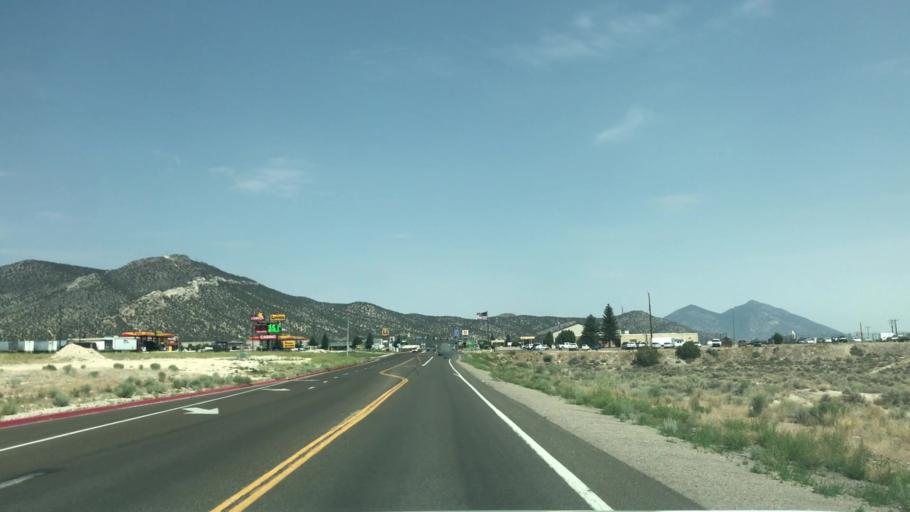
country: US
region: Nevada
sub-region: White Pine County
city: Ely
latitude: 39.2391
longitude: -114.8667
